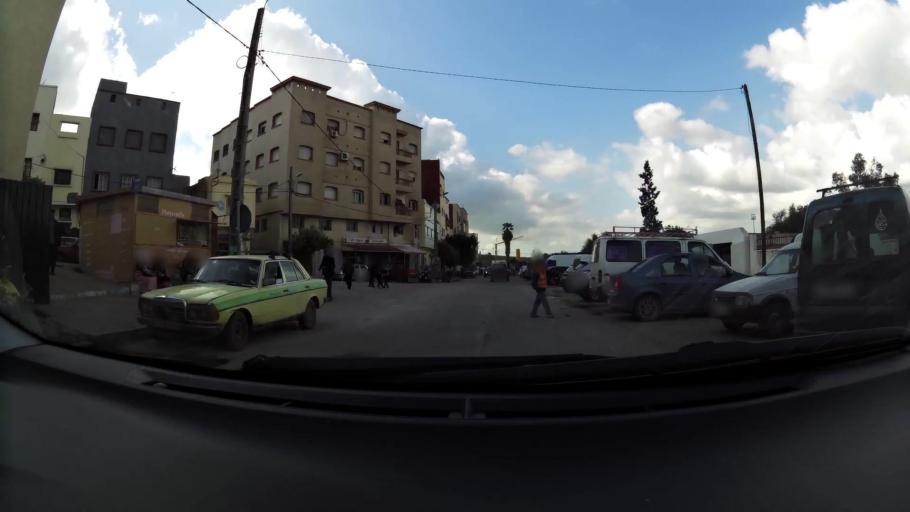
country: MA
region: Chaouia-Ouardigha
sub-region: Settat Province
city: Settat
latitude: 33.0077
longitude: -7.6223
